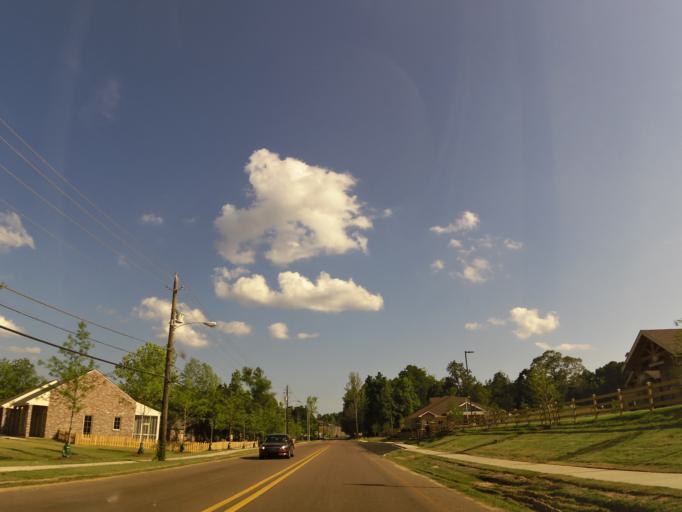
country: US
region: Mississippi
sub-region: Lafayette County
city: University
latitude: 34.3407
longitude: -89.5203
